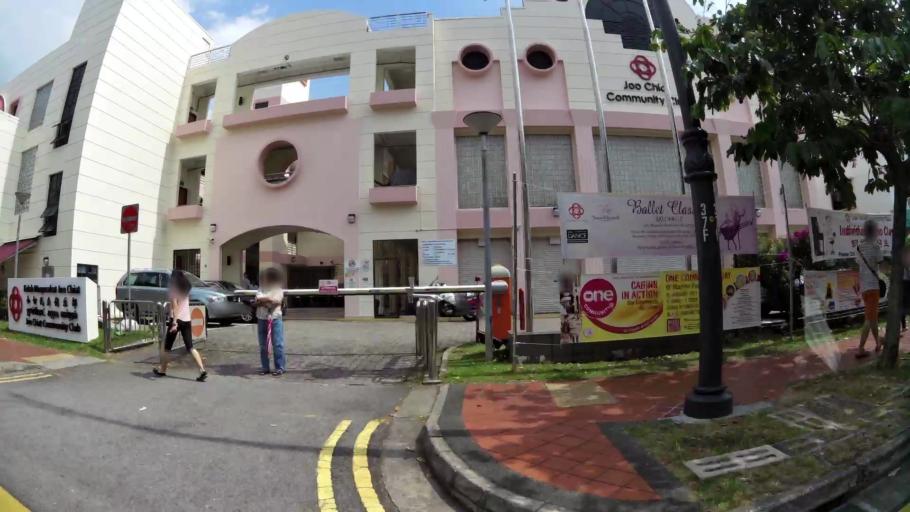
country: SG
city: Singapore
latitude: 1.3073
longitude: 103.9041
